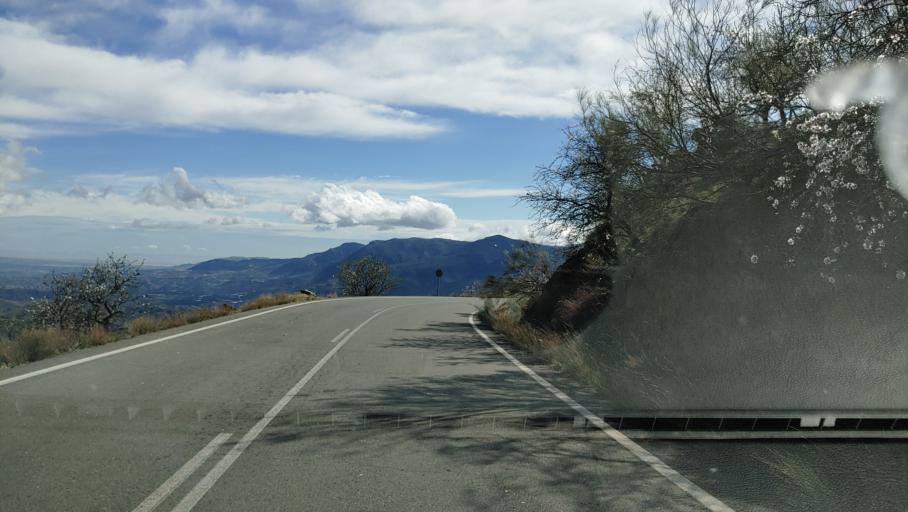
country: ES
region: Andalusia
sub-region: Provincia de Almeria
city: Ohanes
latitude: 37.0404
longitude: -2.7322
